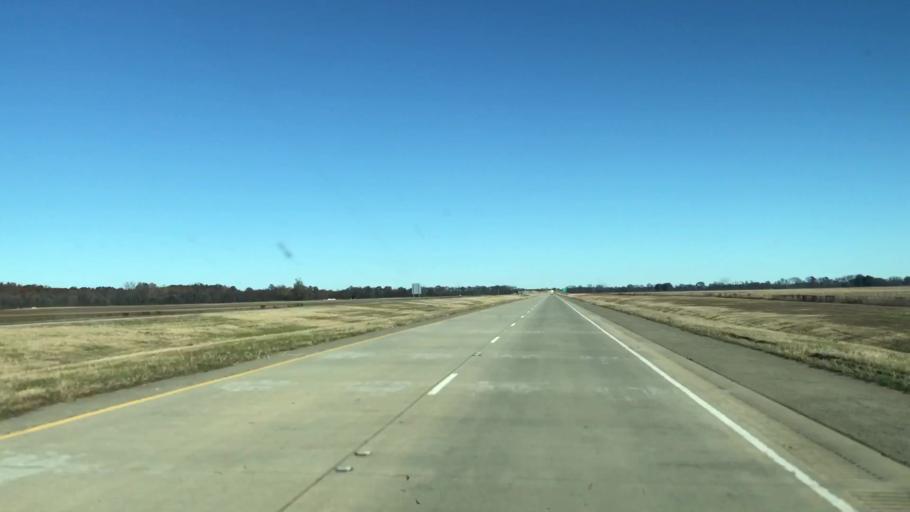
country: US
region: Louisiana
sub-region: Caddo Parish
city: Vivian
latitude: 32.8678
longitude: -93.8601
